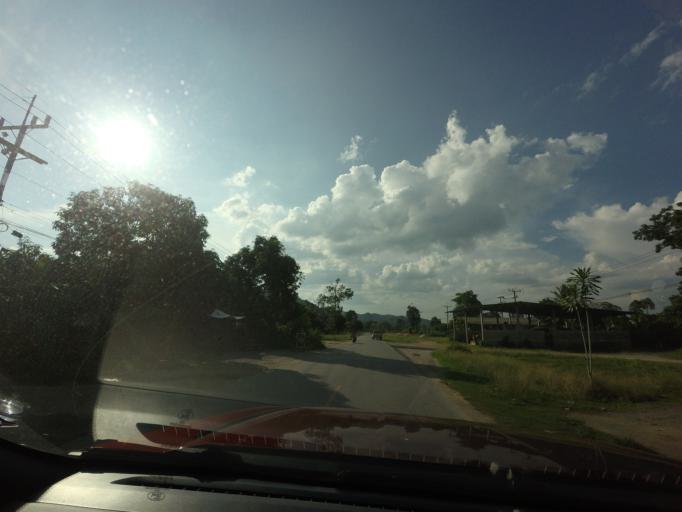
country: TH
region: Yala
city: Than To
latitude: 6.1808
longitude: 101.2641
